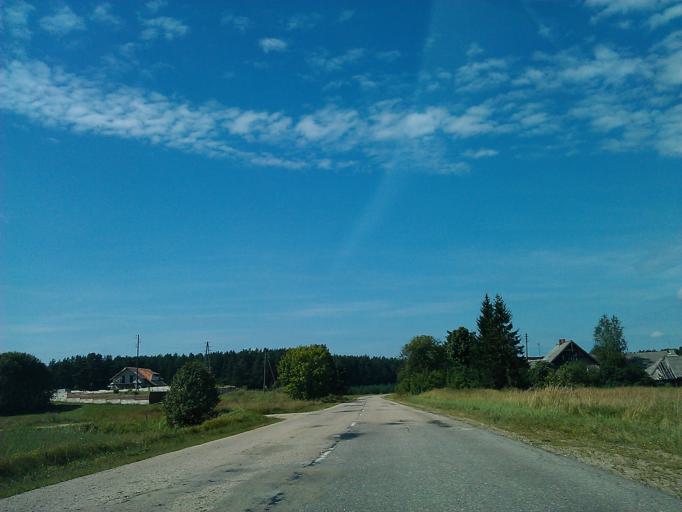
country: LV
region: Ropazu
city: Ropazi
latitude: 56.9419
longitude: 24.6089
